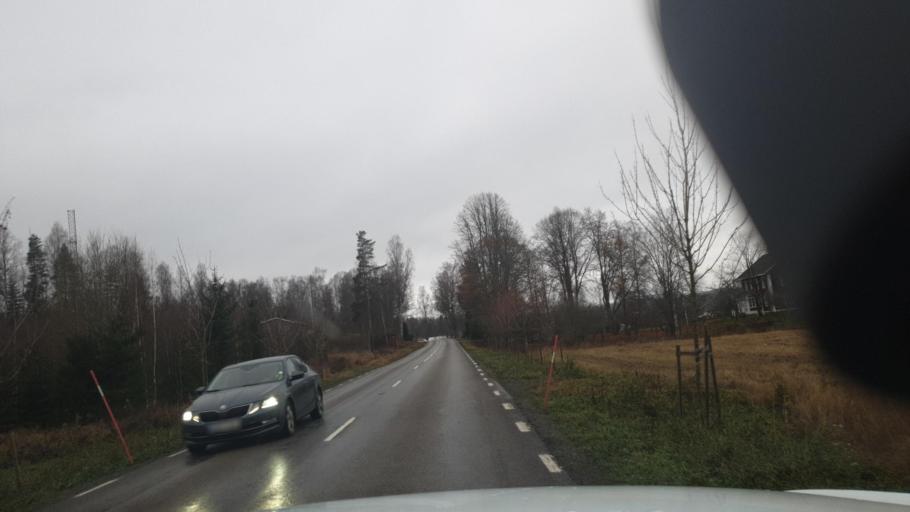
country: SE
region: Vaermland
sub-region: Arvika Kommun
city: Arvika
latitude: 59.6457
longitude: 12.4709
